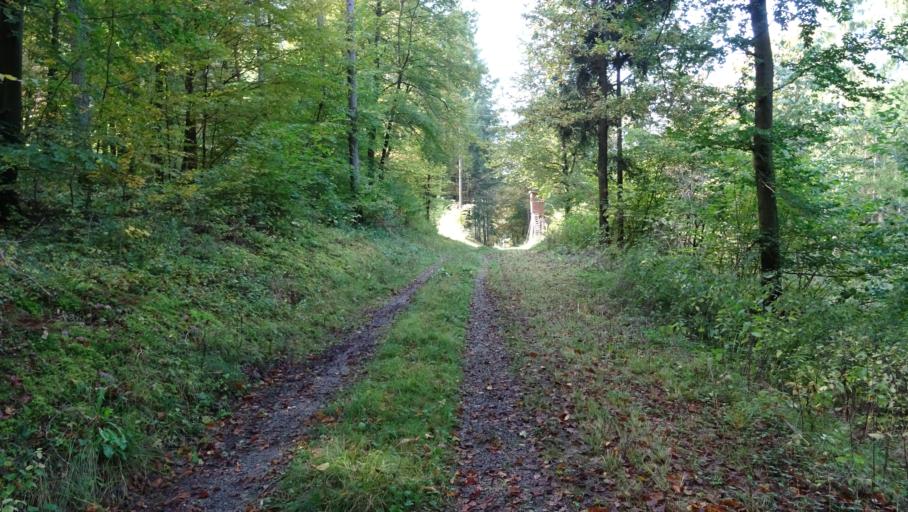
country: DE
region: Baden-Wuerttemberg
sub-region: Karlsruhe Region
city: Billigheim
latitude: 49.3685
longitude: 9.2693
